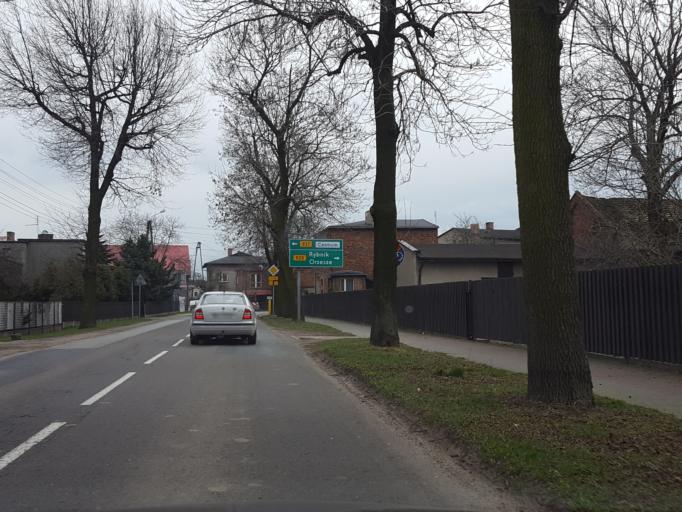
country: PL
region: Silesian Voivodeship
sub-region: Powiat mikolowski
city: Orzesze
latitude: 50.1877
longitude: 18.8006
